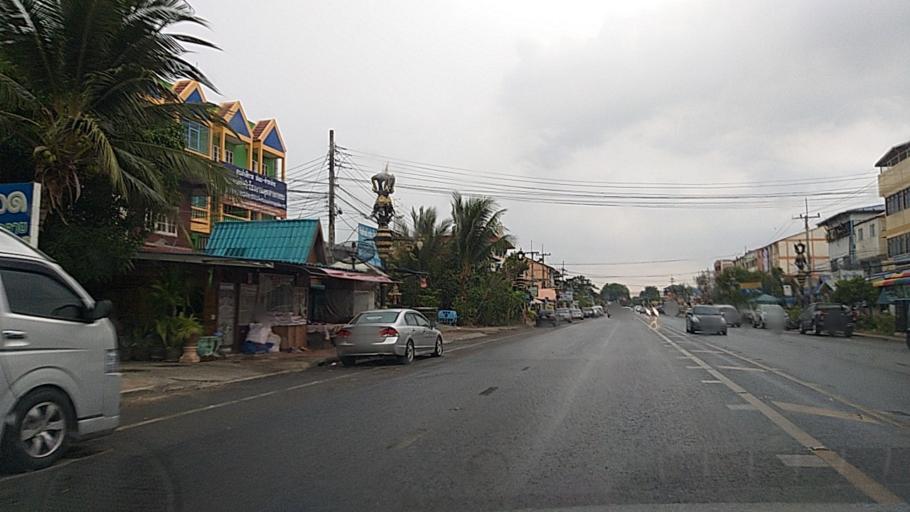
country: TH
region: Phra Nakhon Si Ayutthaya
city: Phra Nakhon Si Ayutthaya
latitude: 14.3438
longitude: 100.5877
